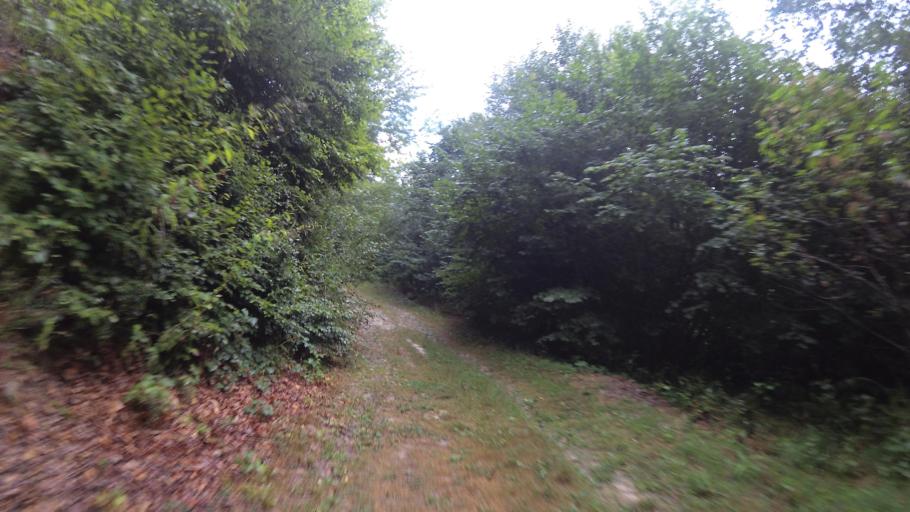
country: DE
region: Rheinland-Pfalz
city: Rorodt
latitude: 49.7648
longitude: 7.1028
